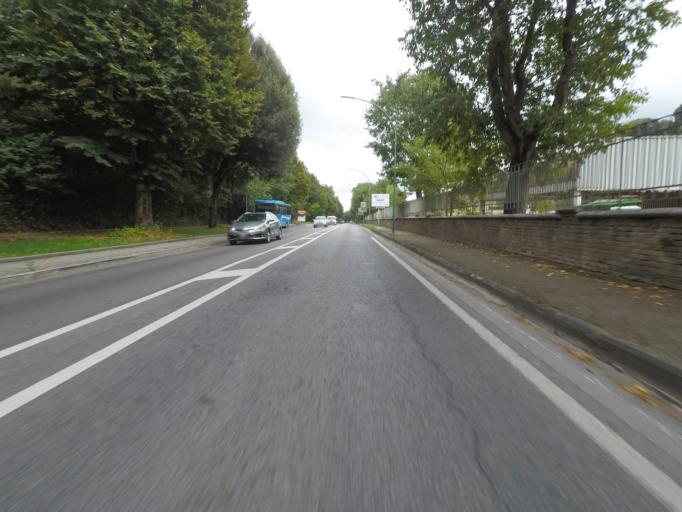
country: IT
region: Tuscany
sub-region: Provincia di Siena
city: Siena
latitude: 43.3261
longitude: 11.3422
